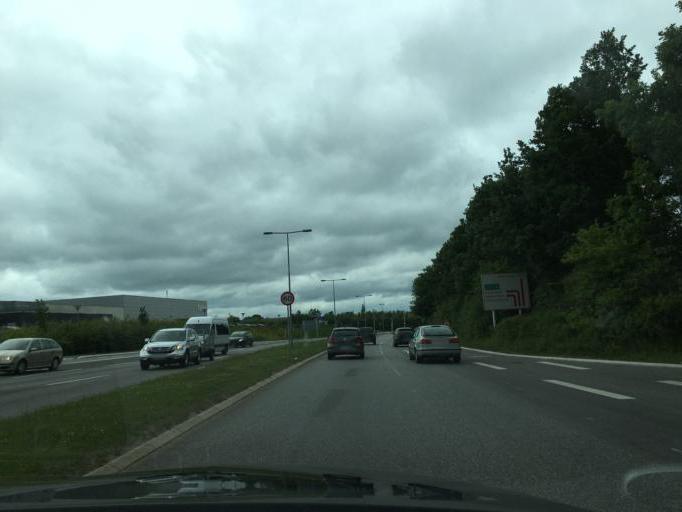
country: DK
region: Capital Region
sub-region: Fredensborg Kommune
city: Kokkedal
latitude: 55.9054
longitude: 12.4769
